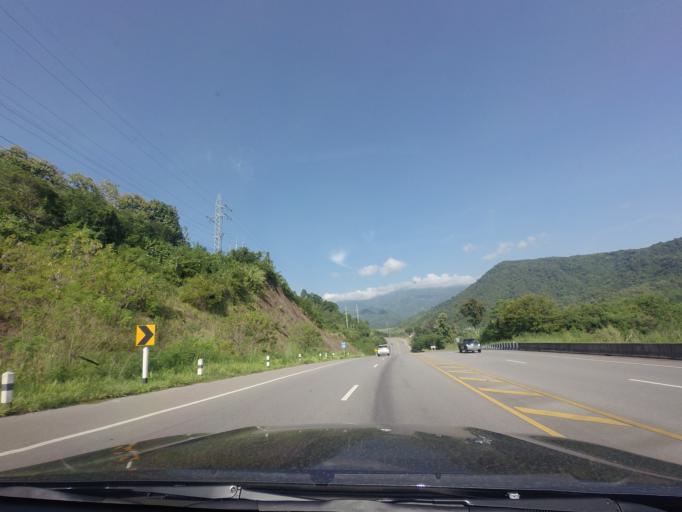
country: TH
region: Phetchabun
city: Lom Sak
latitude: 16.7773
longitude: 101.1117
